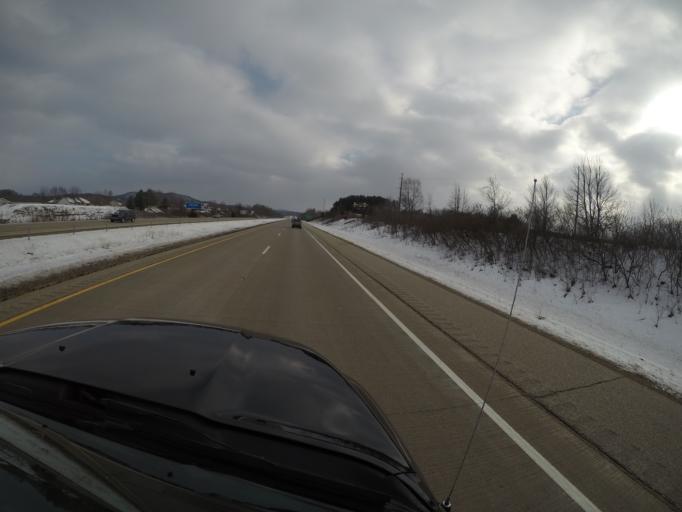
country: US
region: Wisconsin
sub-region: La Crosse County
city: Holmen
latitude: 43.9537
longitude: -91.2779
